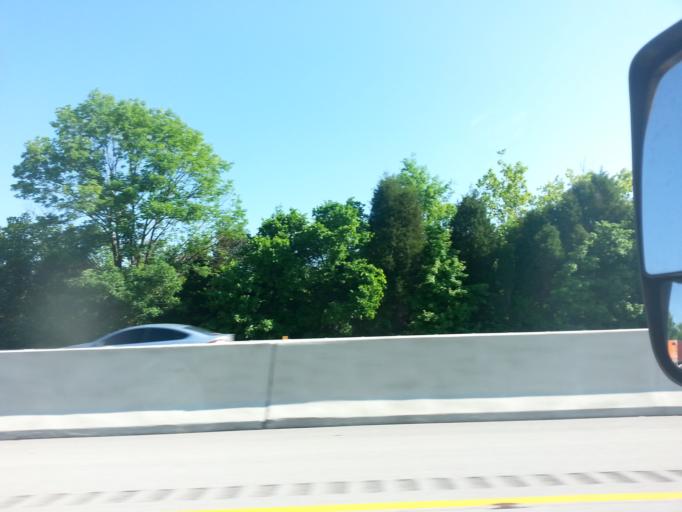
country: US
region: Kentucky
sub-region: Shelby County
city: Simpsonville
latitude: 38.2184
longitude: -85.4239
